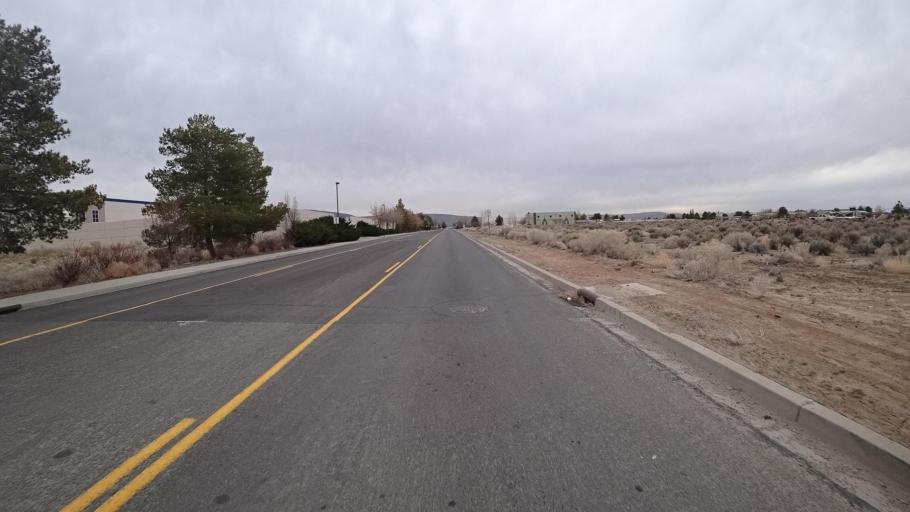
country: US
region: Nevada
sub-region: Washoe County
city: Spanish Springs
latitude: 39.6733
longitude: -119.7068
